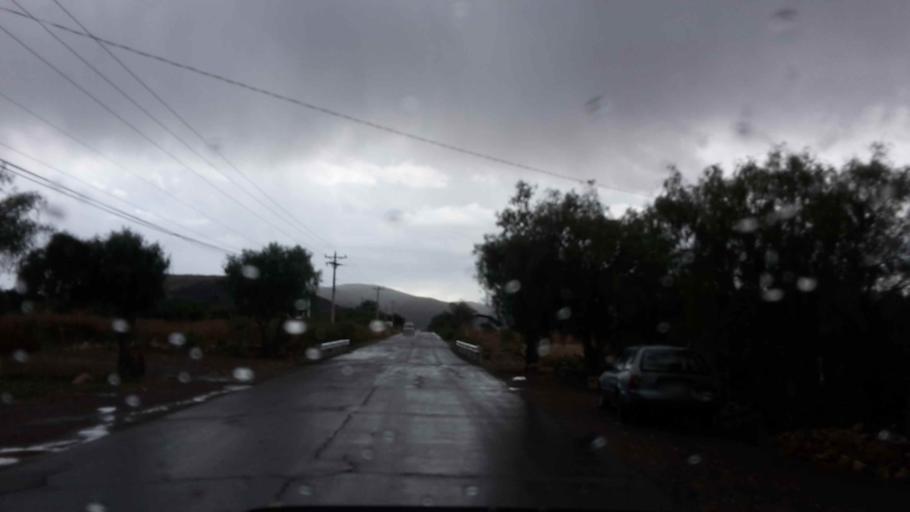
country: BO
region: Cochabamba
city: Tarata
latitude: -17.5581
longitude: -66.0854
